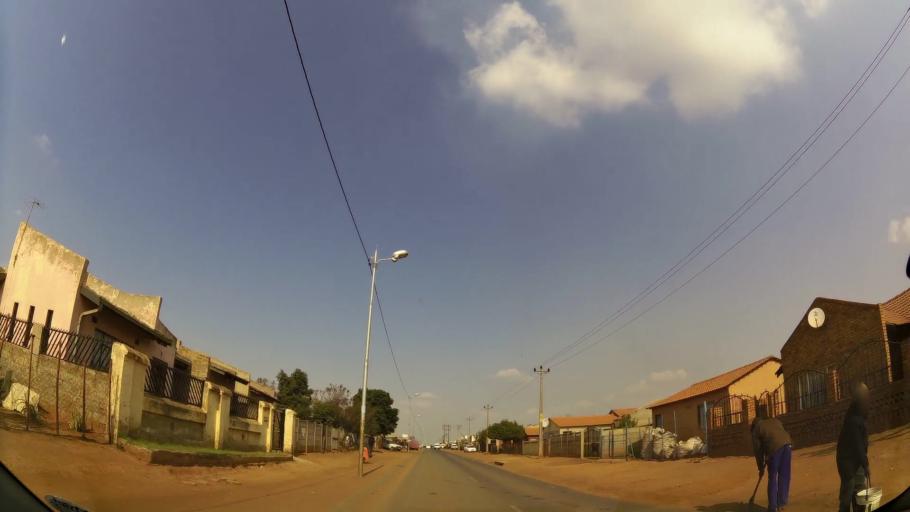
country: ZA
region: Gauteng
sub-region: Ekurhuleni Metropolitan Municipality
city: Springs
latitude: -26.1145
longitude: 28.4850
